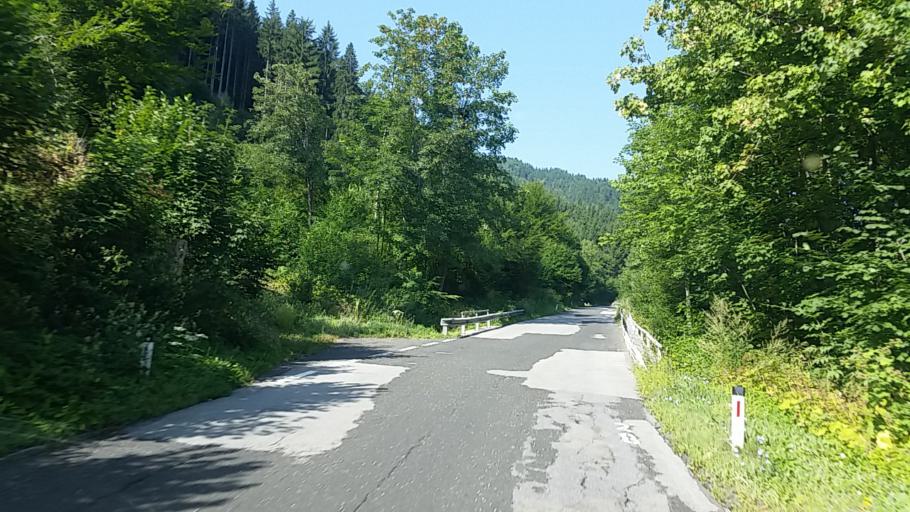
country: AT
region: Carinthia
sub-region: Politischer Bezirk Villach Land
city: Arnoldstein
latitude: 46.5383
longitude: 13.7657
